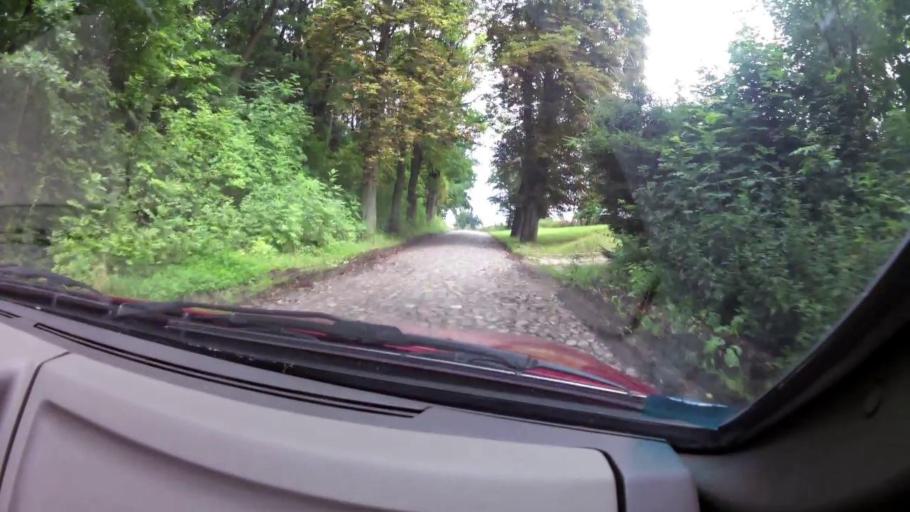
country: PL
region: West Pomeranian Voivodeship
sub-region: Powiat swidwinski
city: Polczyn-Zdroj
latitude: 53.7932
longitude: 16.0421
